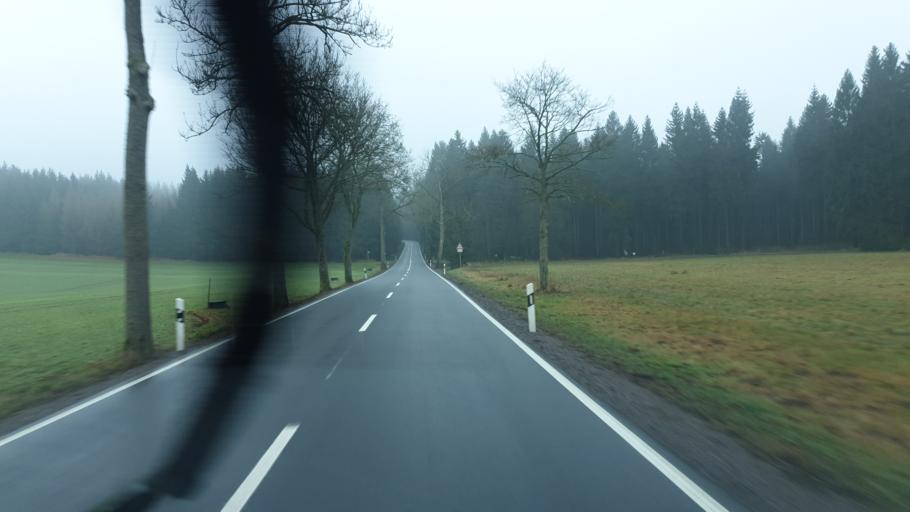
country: DE
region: Saxony
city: Sayda
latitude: 50.7005
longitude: 13.4425
